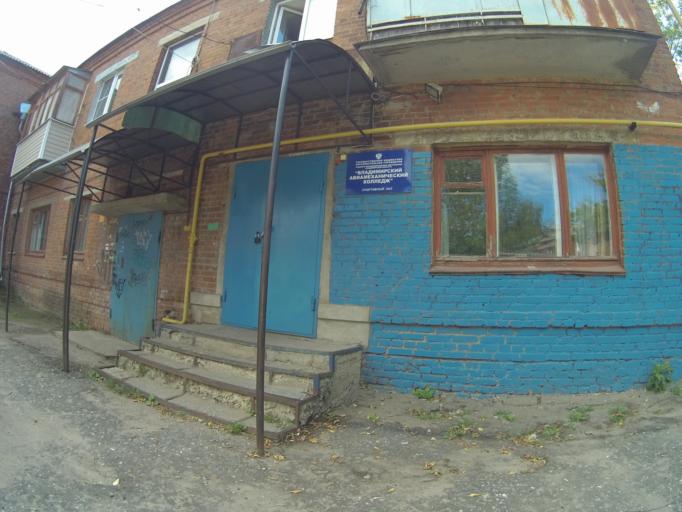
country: RU
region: Vladimir
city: Vladimir
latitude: 56.1192
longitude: 40.3778
